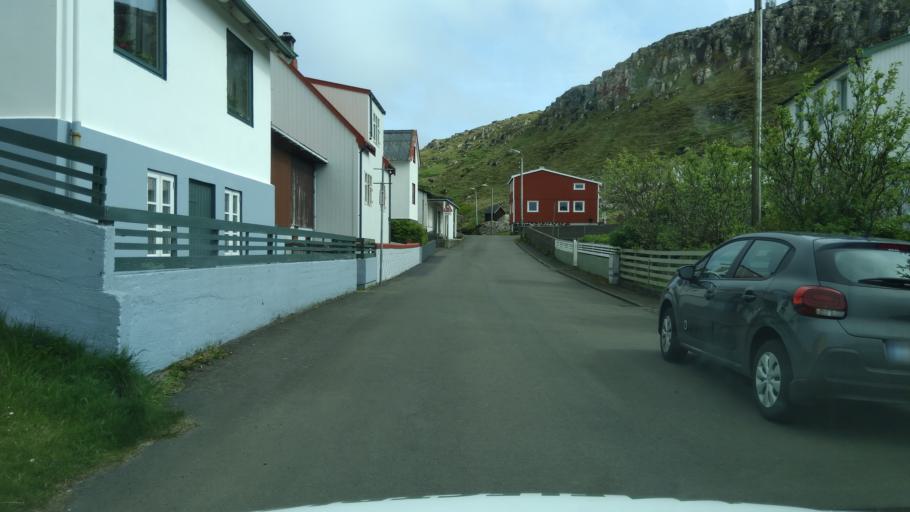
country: FO
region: Sandoy
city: Sandur
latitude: 61.9028
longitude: -6.8855
